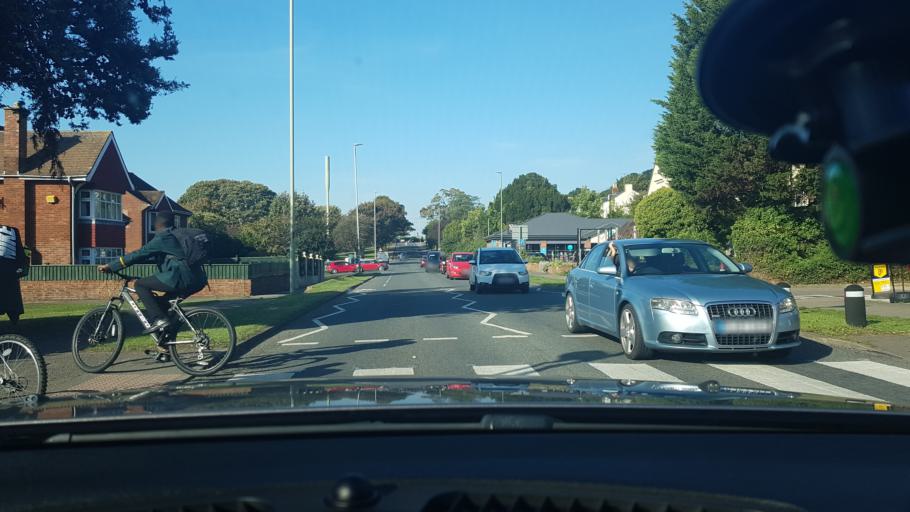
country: GB
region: England
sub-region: Gloucestershire
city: Gloucester
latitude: 51.8311
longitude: -2.2452
